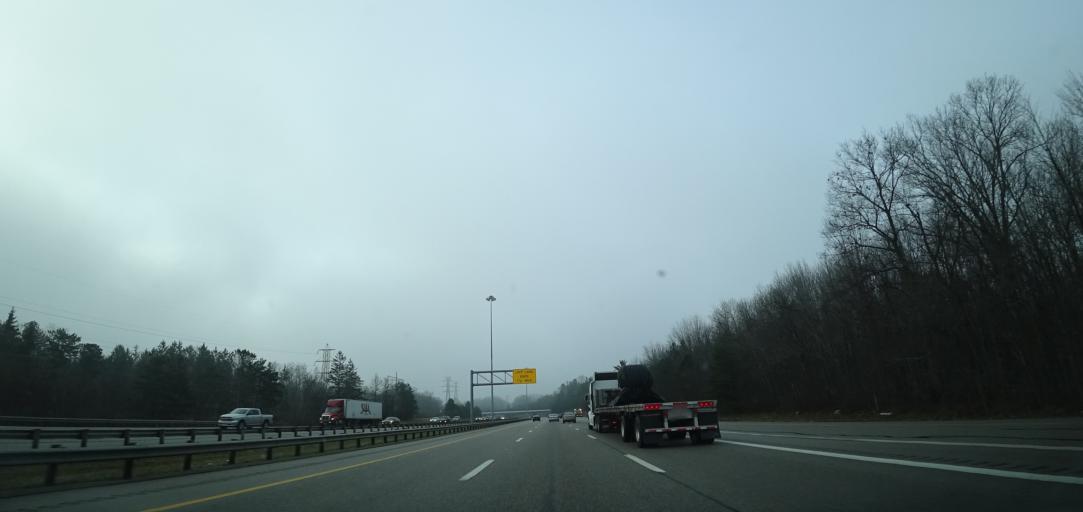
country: US
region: Ohio
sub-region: Cuyahoga County
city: Brecksville
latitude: 41.3120
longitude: -81.6492
